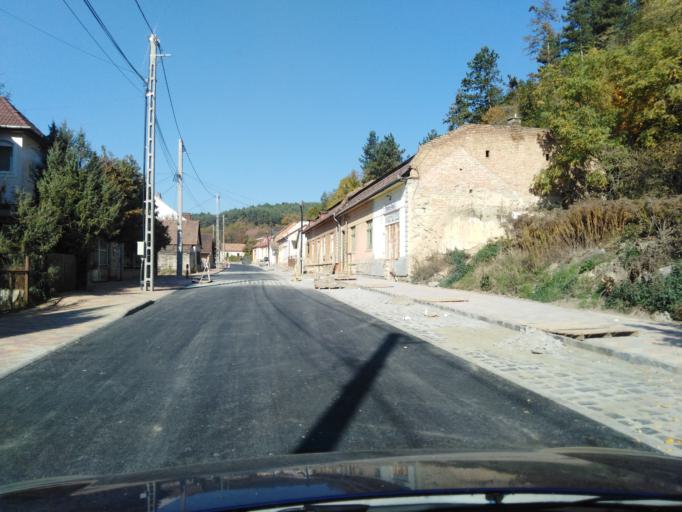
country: HU
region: Nograd
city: Salgotarjan
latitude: 48.1053
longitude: 19.8013
